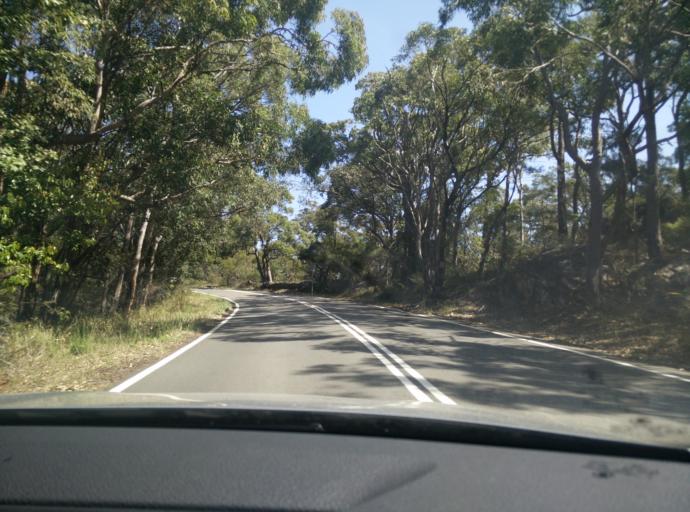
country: AU
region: New South Wales
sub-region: Gosford Shire
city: Umina
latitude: -33.5367
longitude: 151.3027
